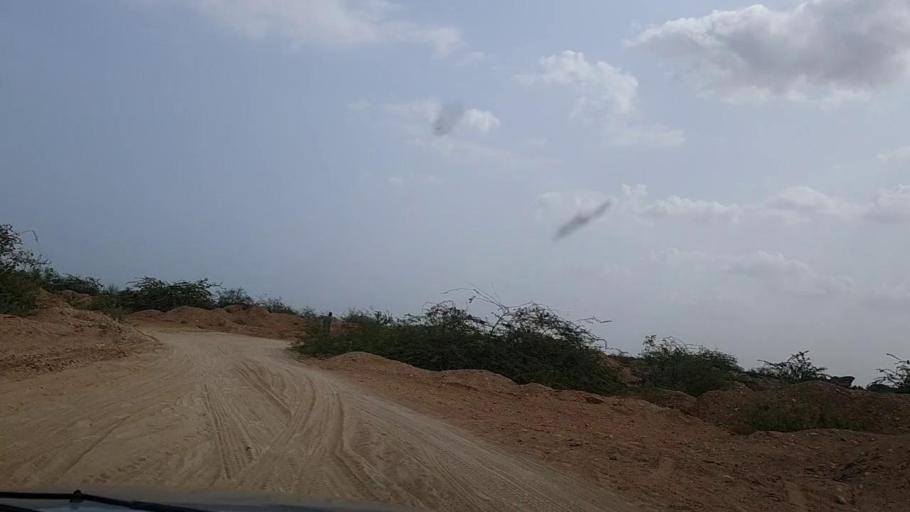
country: PK
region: Sindh
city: Kotri
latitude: 25.2809
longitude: 68.2663
